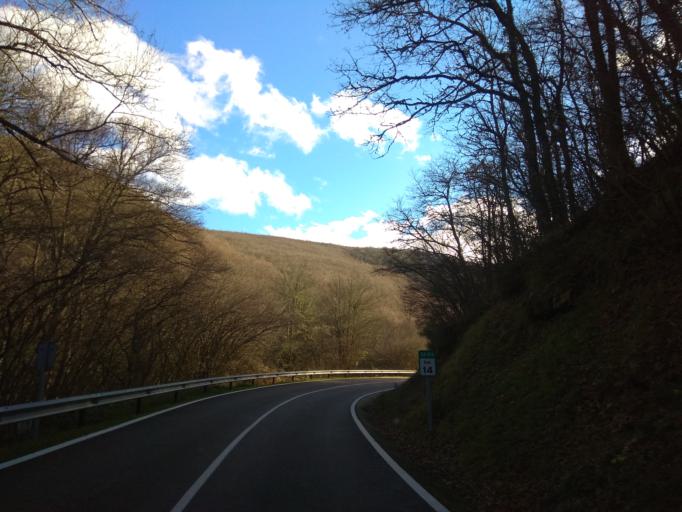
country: ES
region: Cantabria
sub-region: Provincia de Cantabria
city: San Martin de Elines
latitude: 42.8700
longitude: -3.9125
